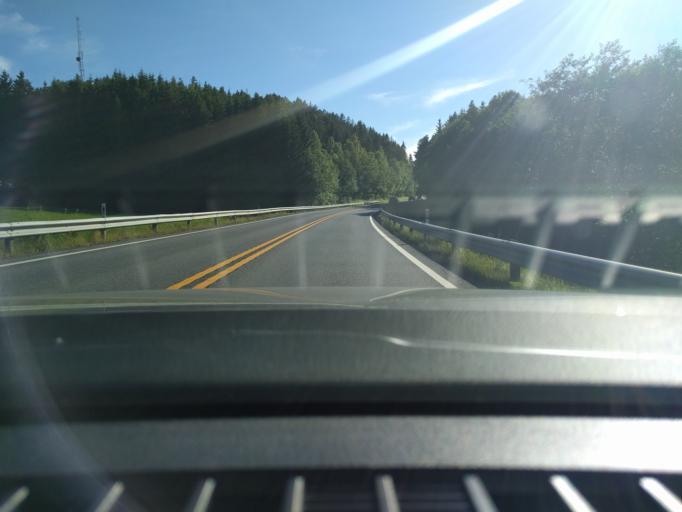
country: NO
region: Buskerud
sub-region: Royken
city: Royken
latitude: 59.7383
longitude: 10.3720
